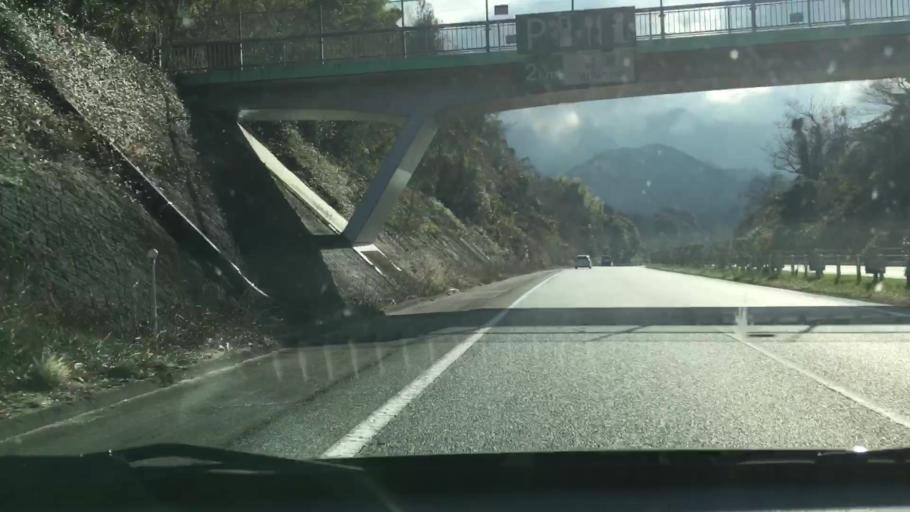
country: JP
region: Kumamoto
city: Matsubase
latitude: 32.5552
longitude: 130.6950
